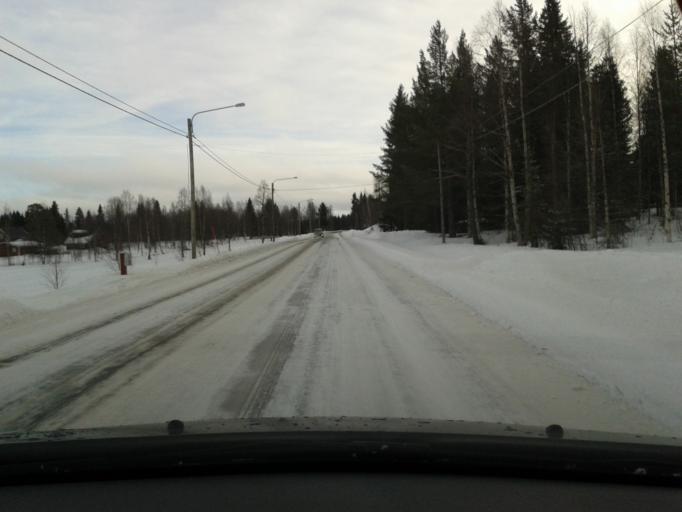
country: SE
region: Vaesterbotten
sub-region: Vilhelmina Kommun
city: Sjoberg
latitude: 64.6477
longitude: 16.3431
